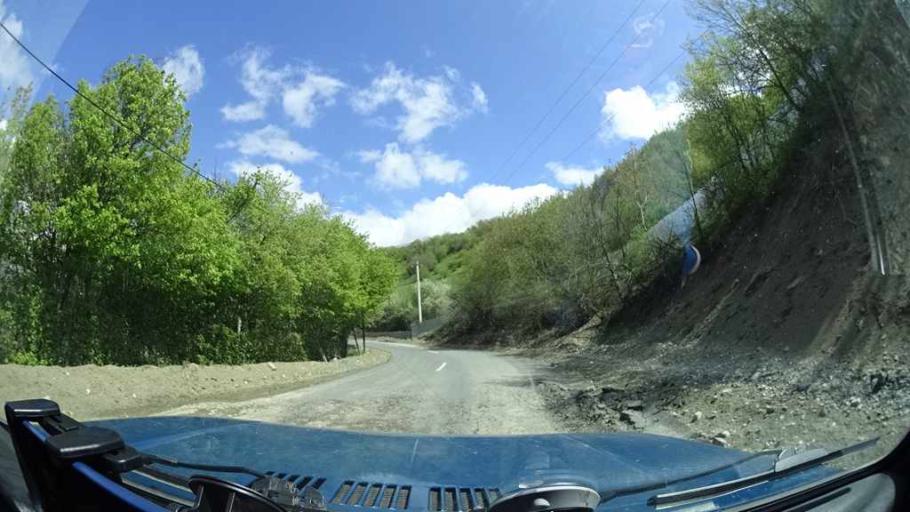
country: AZ
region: Ismayilli
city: Basqal
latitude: 40.8424
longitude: 48.3726
